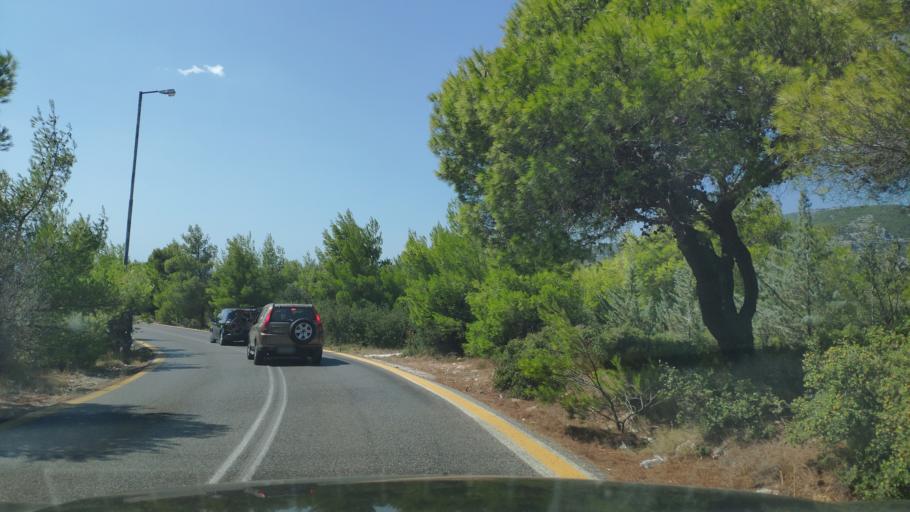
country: GR
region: Attica
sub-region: Nomarchia Anatolikis Attikis
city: Thrakomakedones
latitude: 38.1327
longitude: 23.7417
